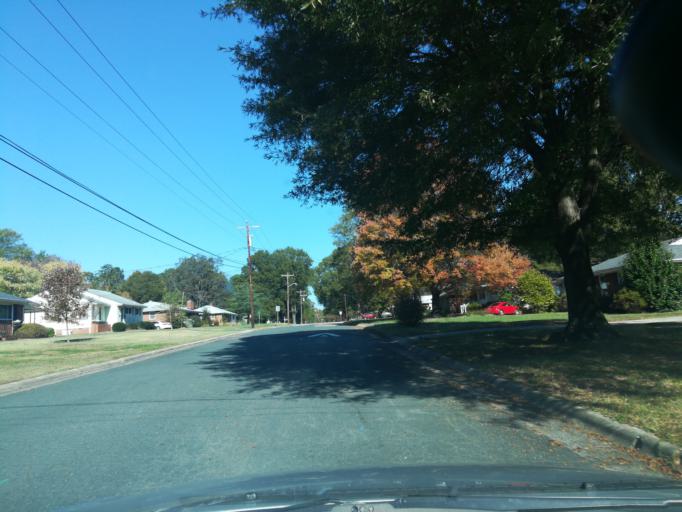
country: US
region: North Carolina
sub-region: Durham County
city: Durham
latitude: 36.0419
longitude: -78.9072
